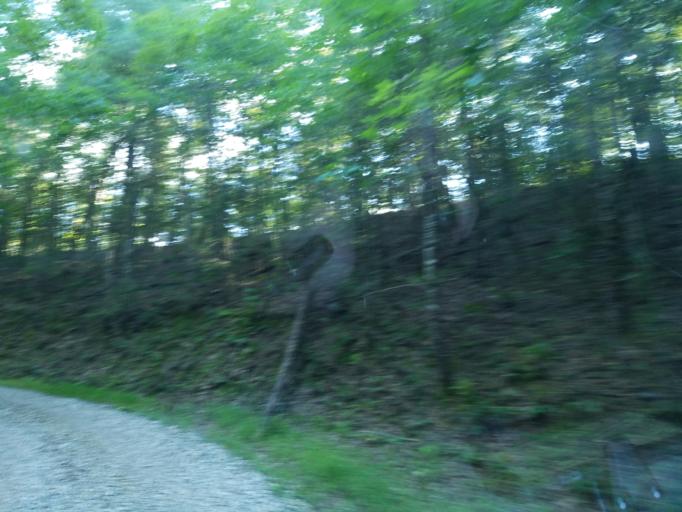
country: US
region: Georgia
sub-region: Union County
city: Blairsville
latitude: 34.7620
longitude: -84.1169
